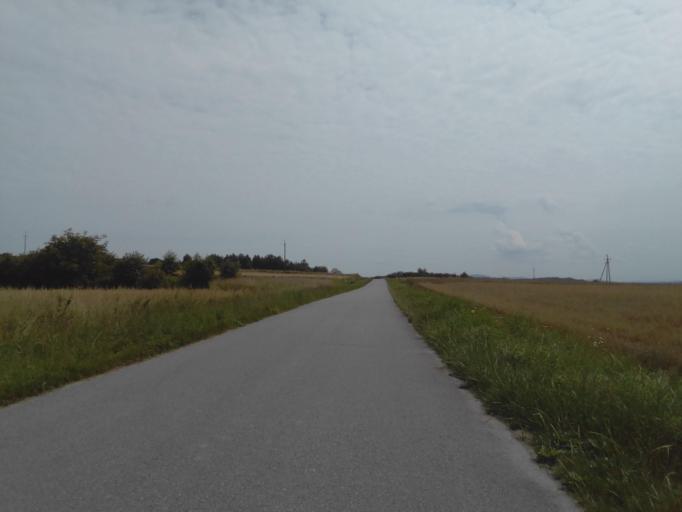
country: PL
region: Subcarpathian Voivodeship
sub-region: Powiat jasielski
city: Tarnowiec
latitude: 49.7760
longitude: 21.6008
